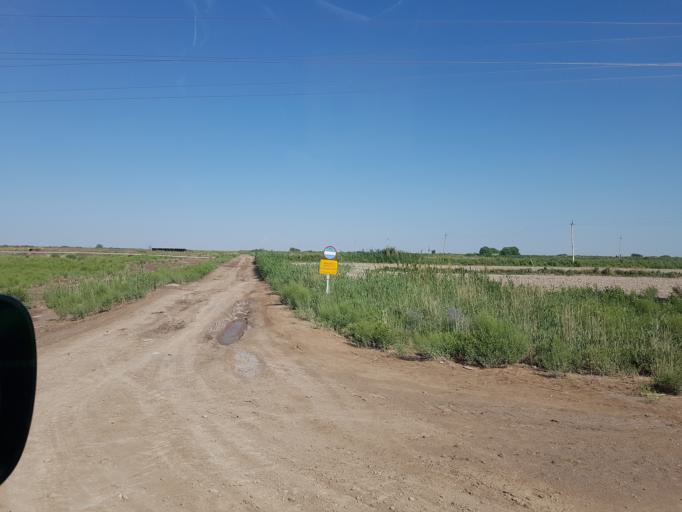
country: TM
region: Dasoguz
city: Koeneuergench
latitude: 42.1352
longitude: 58.9527
